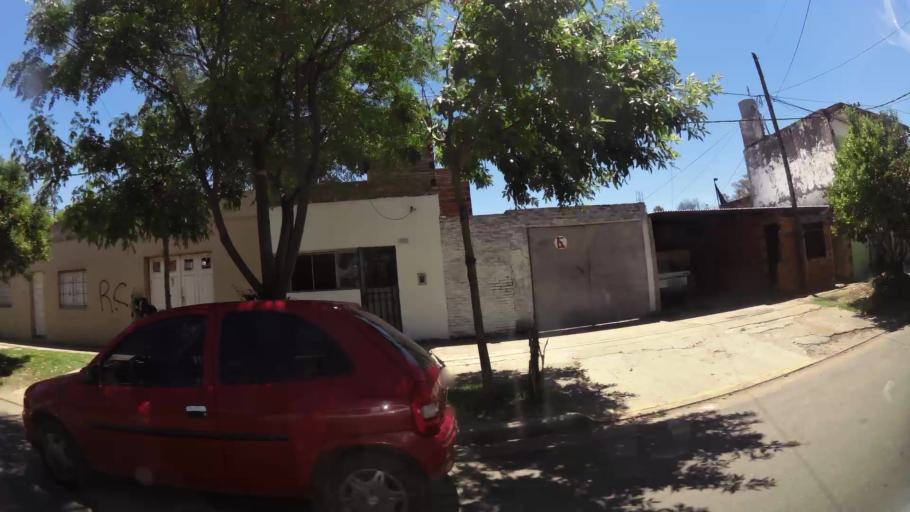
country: AR
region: Santa Fe
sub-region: Departamento de Rosario
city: Rosario
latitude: -32.9544
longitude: -60.7070
